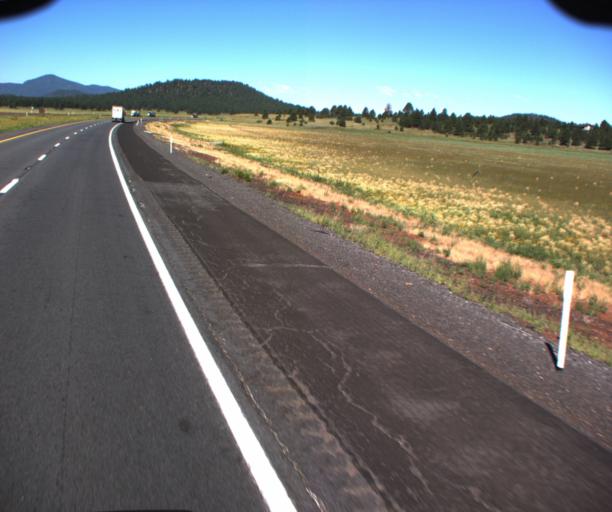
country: US
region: Arizona
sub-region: Coconino County
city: Williams
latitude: 35.2597
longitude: -112.0758
